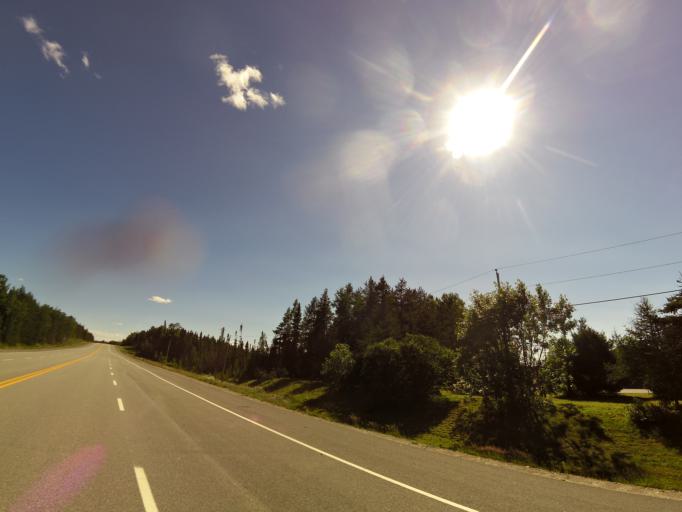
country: CA
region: Quebec
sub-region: Abitibi-Temiscamingue
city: Val-d'Or
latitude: 47.8706
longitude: -77.3525
